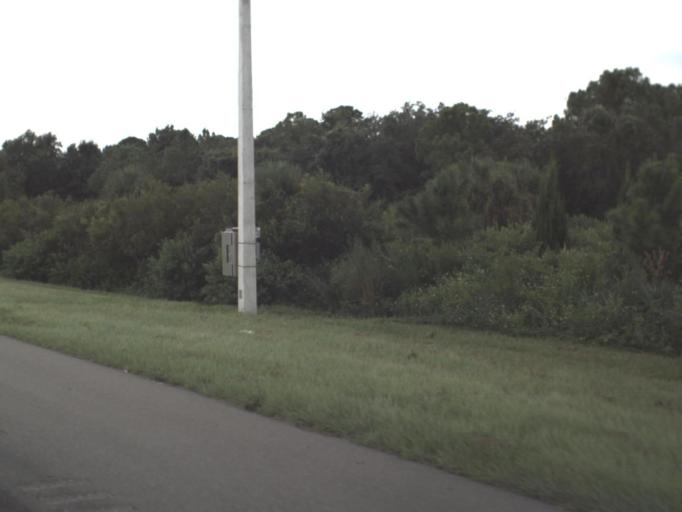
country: US
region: Florida
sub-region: Sarasota County
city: Nokomis
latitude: 27.1252
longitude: -82.3999
